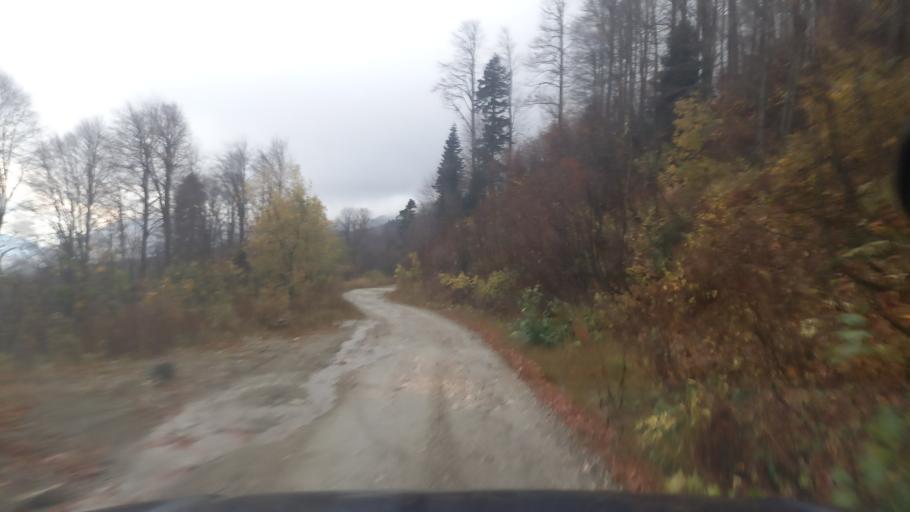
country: RU
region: Krasnodarskiy
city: Dagomys
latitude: 43.9908
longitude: 39.8537
